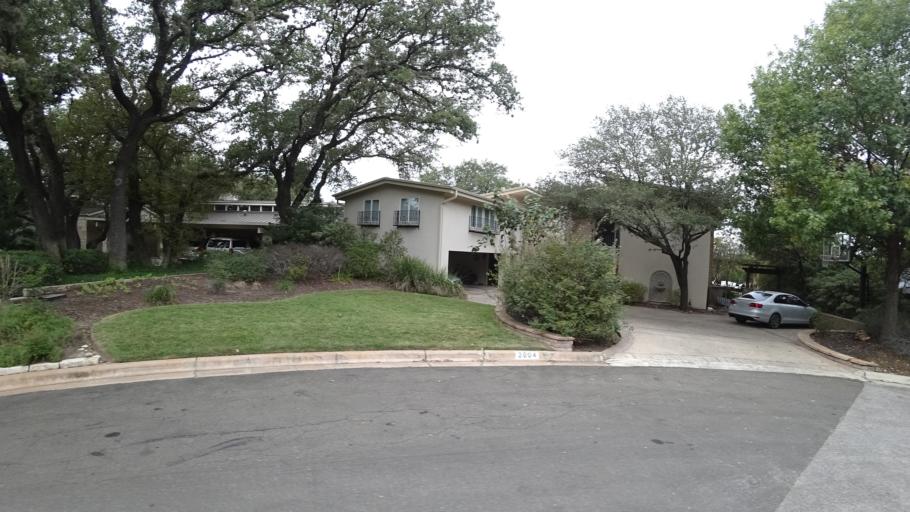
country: US
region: Texas
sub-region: Travis County
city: West Lake Hills
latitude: 30.3050
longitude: -97.7680
